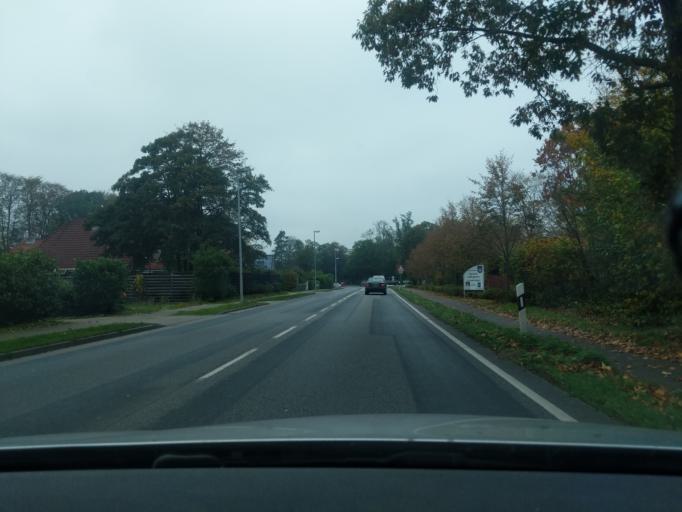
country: DE
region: Lower Saxony
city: Himmelpforten
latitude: 53.6110
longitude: 9.3136
